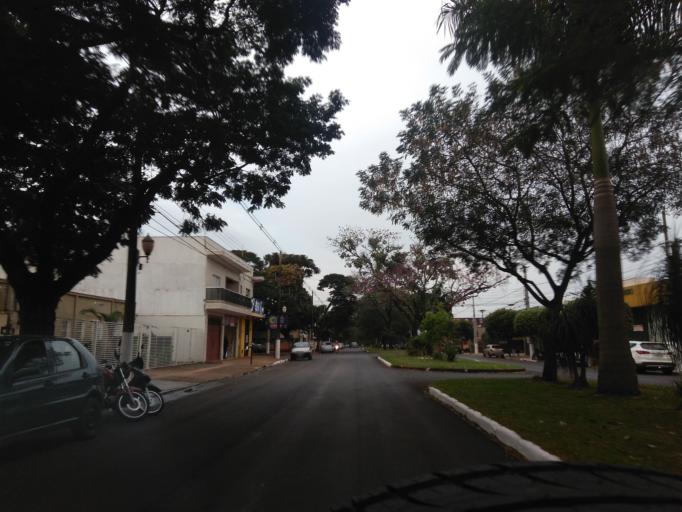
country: BR
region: Mato Grosso do Sul
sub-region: Dourados
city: Dourados
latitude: -22.2321
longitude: -54.8068
